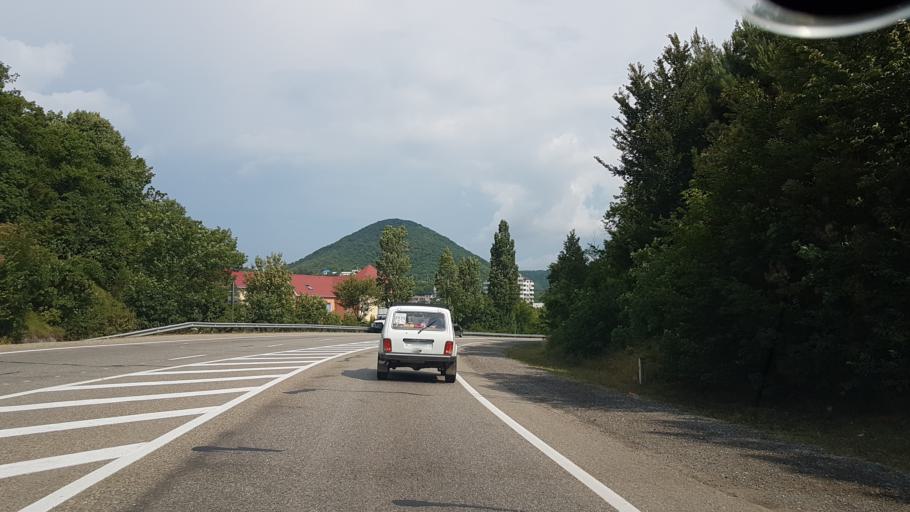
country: RU
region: Krasnodarskiy
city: Ol'ginka
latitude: 44.1899
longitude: 38.8893
